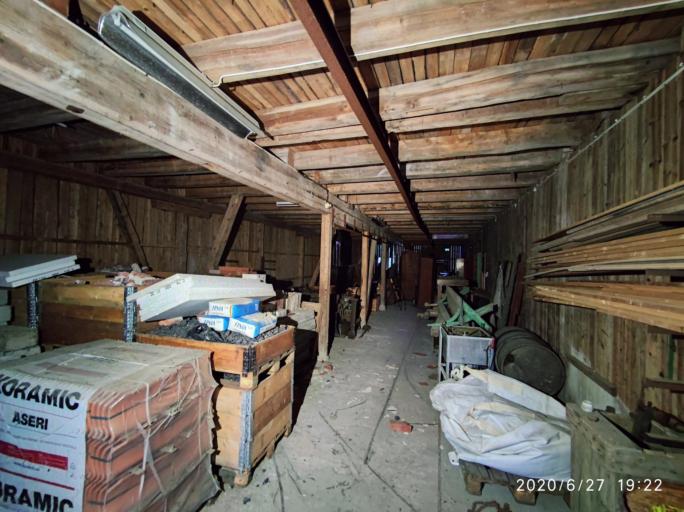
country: NO
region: Buskerud
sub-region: Kongsberg
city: Kongsberg
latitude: 59.6301
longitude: 9.5957
